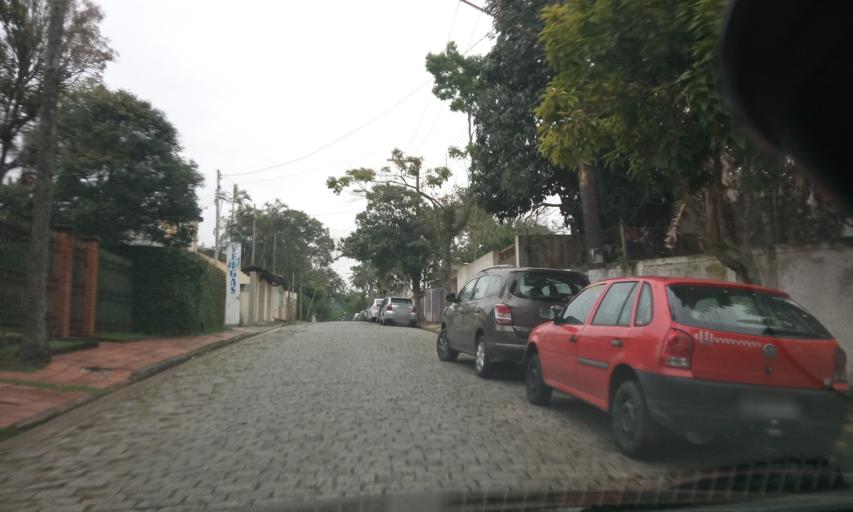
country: BR
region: Sao Paulo
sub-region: Sao Bernardo Do Campo
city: Sao Bernardo do Campo
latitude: -23.7788
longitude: -46.5352
